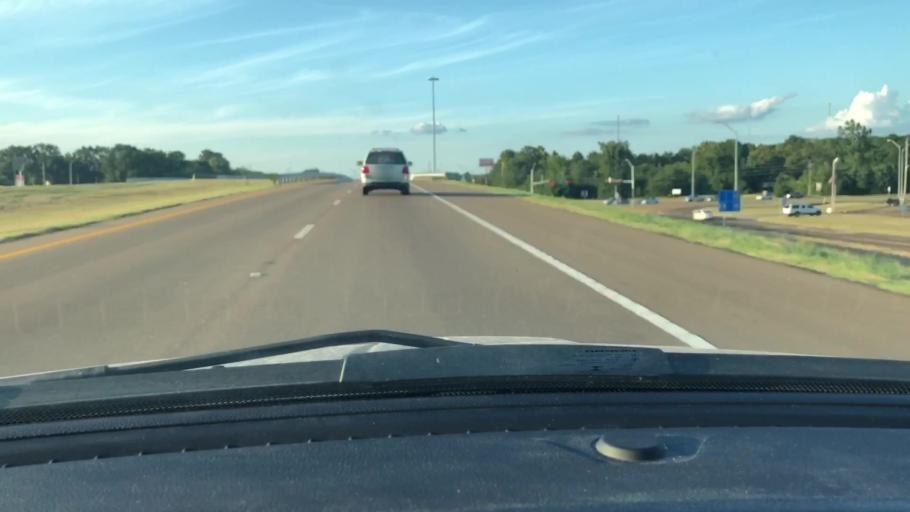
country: US
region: Texas
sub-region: Bowie County
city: Wake Village
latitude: 33.4171
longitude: -94.0966
